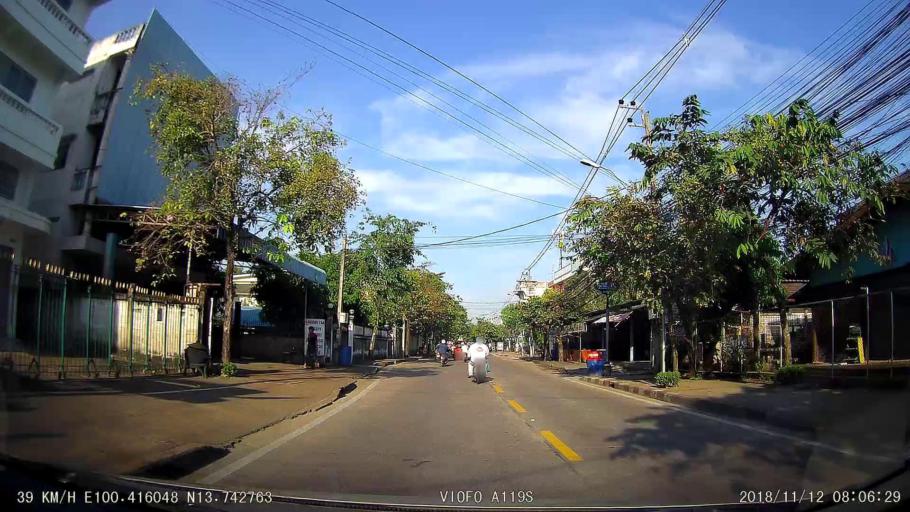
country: TH
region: Bangkok
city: Phasi Charoen
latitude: 13.7428
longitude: 100.4159
